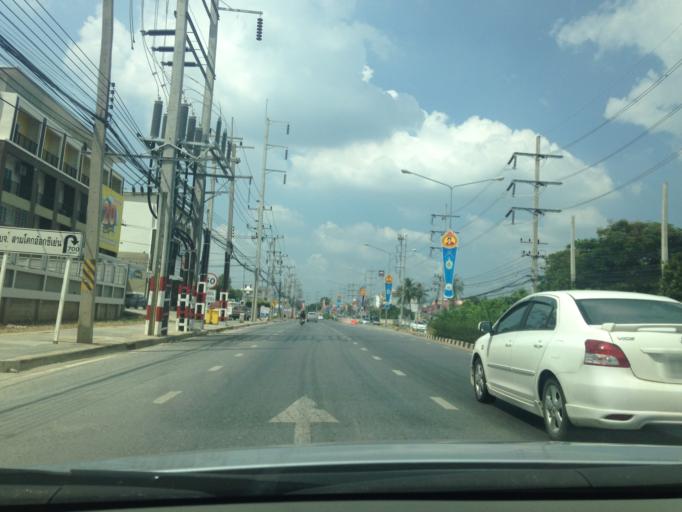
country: TH
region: Pathum Thani
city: Sam Khok
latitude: 14.0638
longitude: 100.5235
